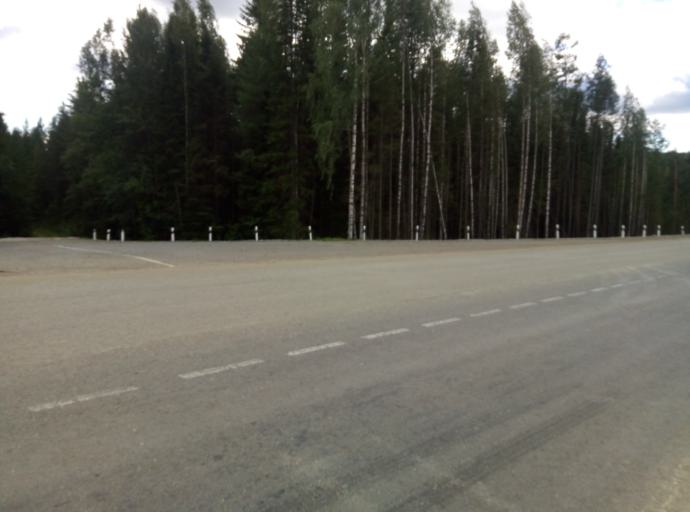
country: RU
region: Sverdlovsk
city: Karpinsk
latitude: 59.6524
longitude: 59.7059
